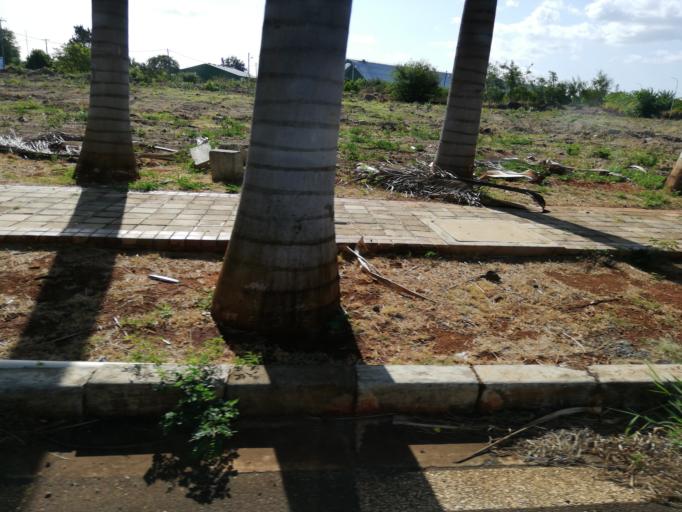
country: MU
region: Port Louis
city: Port Louis
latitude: -20.1602
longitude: 57.4916
